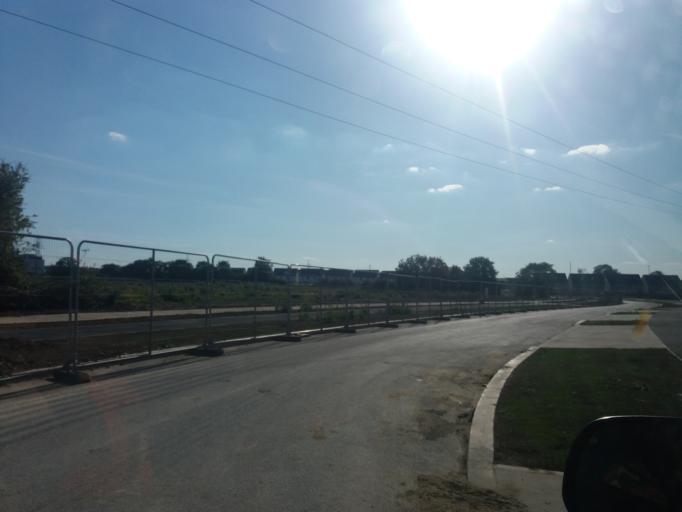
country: IE
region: Leinster
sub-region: Fingal County
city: Blanchardstown
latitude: 53.4239
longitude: -6.3714
